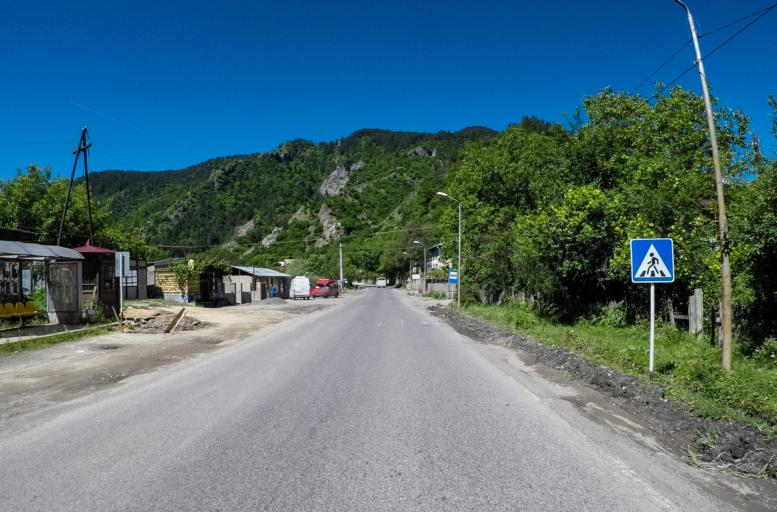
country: GE
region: Samtskhe-Javakheti
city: Borjomi
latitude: 41.8283
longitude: 43.3531
